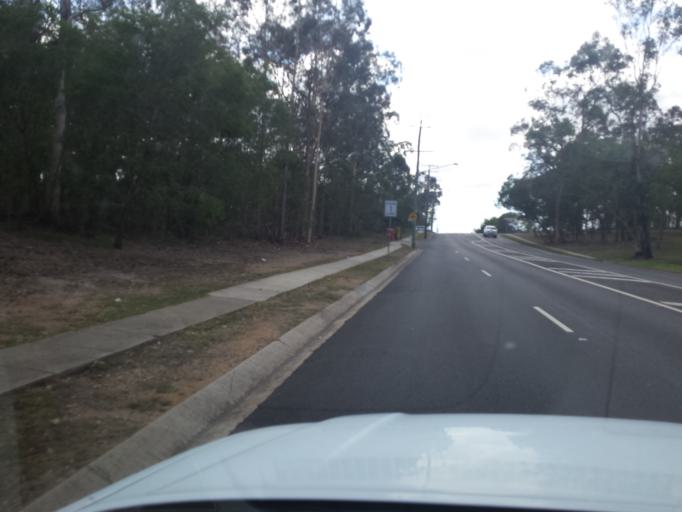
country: AU
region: Queensland
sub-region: Brisbane
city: Stafford Heights
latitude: -27.3889
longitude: 152.9973
